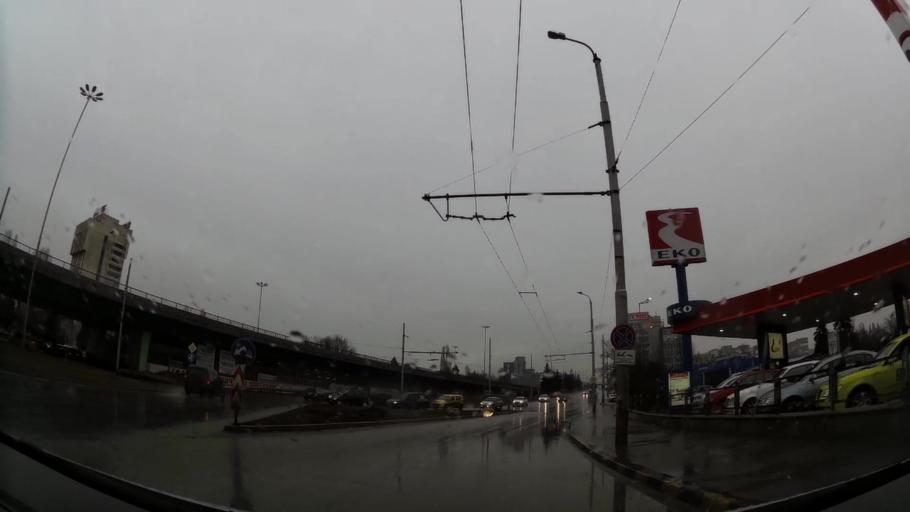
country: BG
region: Sofia-Capital
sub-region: Stolichna Obshtina
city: Sofia
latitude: 42.6680
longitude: 23.3683
